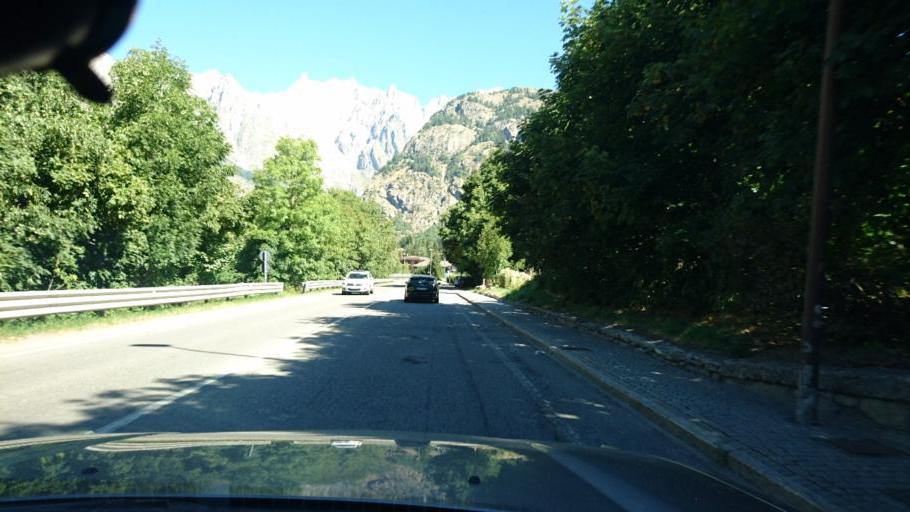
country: IT
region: Aosta Valley
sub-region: Valle d'Aosta
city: Courmayeur
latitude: 45.7882
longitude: 6.9706
